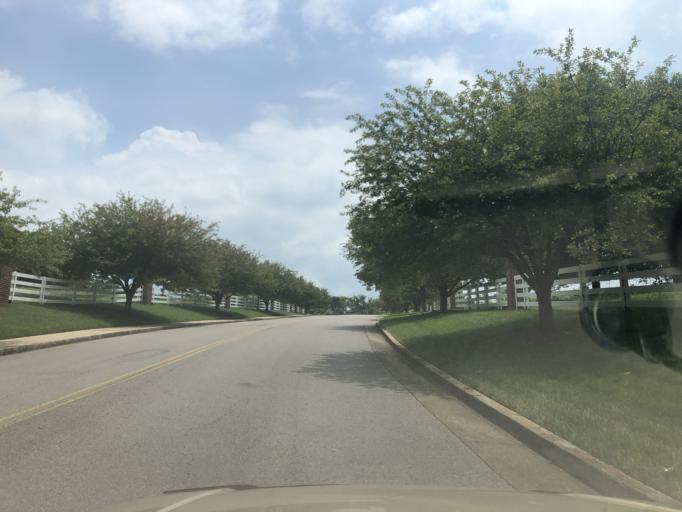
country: US
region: Tennessee
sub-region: Davidson County
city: Lakewood
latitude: 36.2284
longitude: -86.6268
